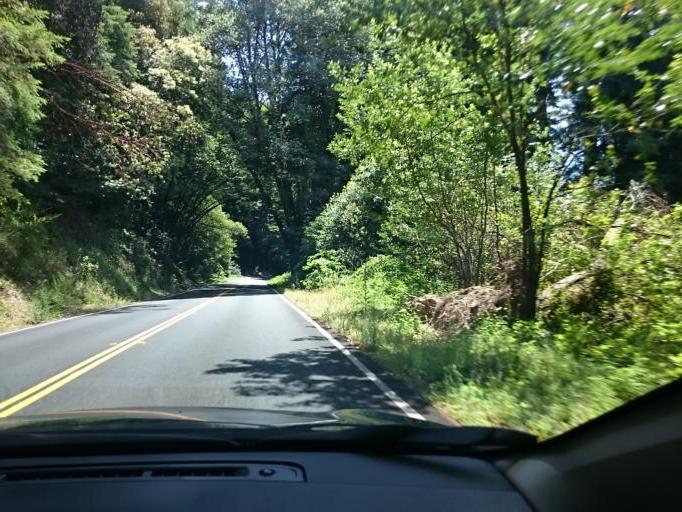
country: US
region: California
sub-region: Mendocino County
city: Fort Bragg
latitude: 39.1784
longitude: -123.6805
